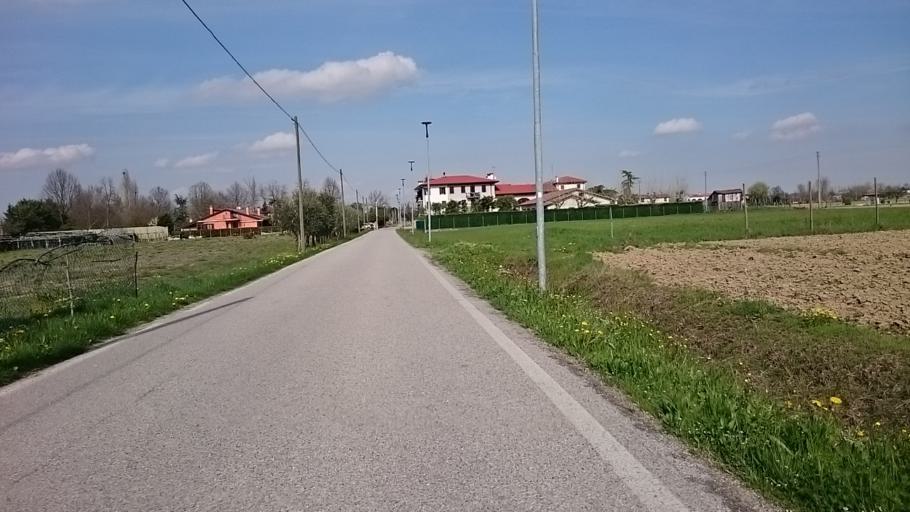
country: IT
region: Veneto
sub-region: Provincia di Padova
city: Montegrotto Terme
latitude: 45.3341
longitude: 11.8002
